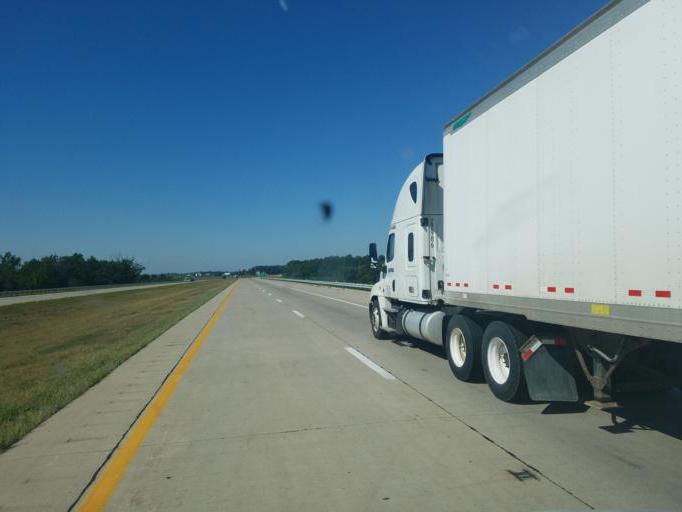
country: US
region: Ohio
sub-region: Crawford County
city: Bucyrus
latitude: 40.8146
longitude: -83.0991
